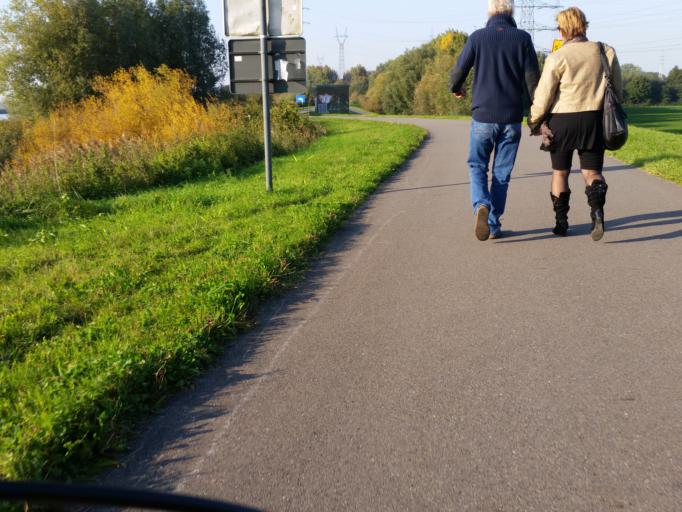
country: BE
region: Flanders
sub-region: Provincie Antwerpen
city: Niel
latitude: 51.1149
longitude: 4.3143
